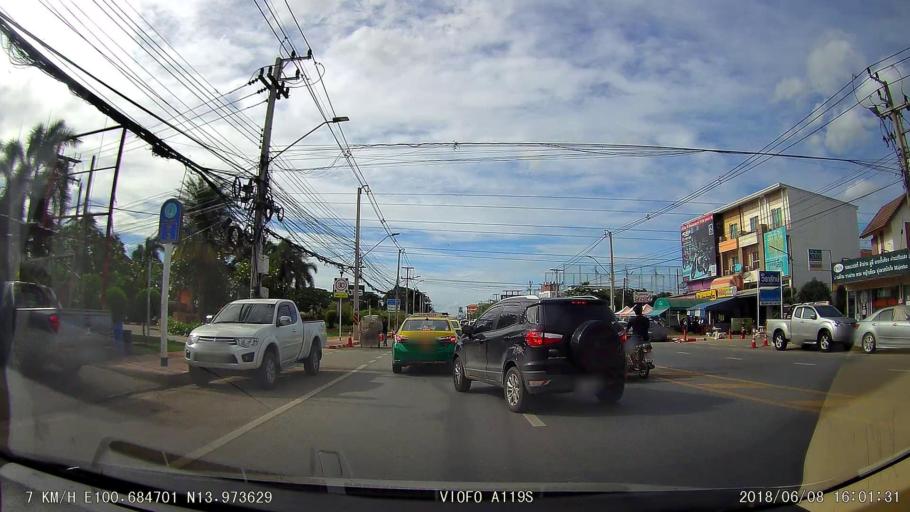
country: TH
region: Bangkok
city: Sai Mai
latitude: 13.9743
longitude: 100.6847
